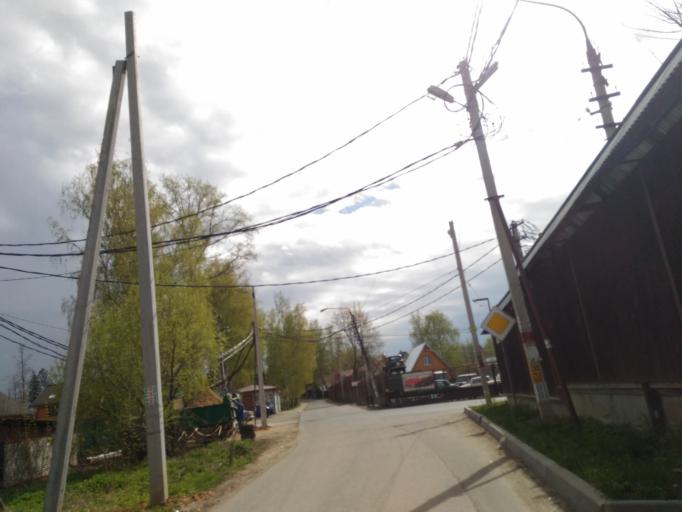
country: RU
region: Moskovskaya
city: Nakhabino
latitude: 55.8490
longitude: 37.1564
